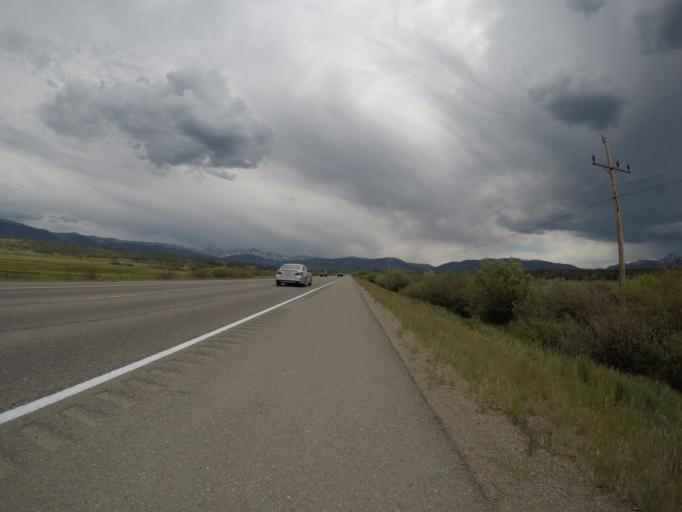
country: US
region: Colorado
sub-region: Grand County
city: Fraser
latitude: 39.9673
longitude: -105.8240
